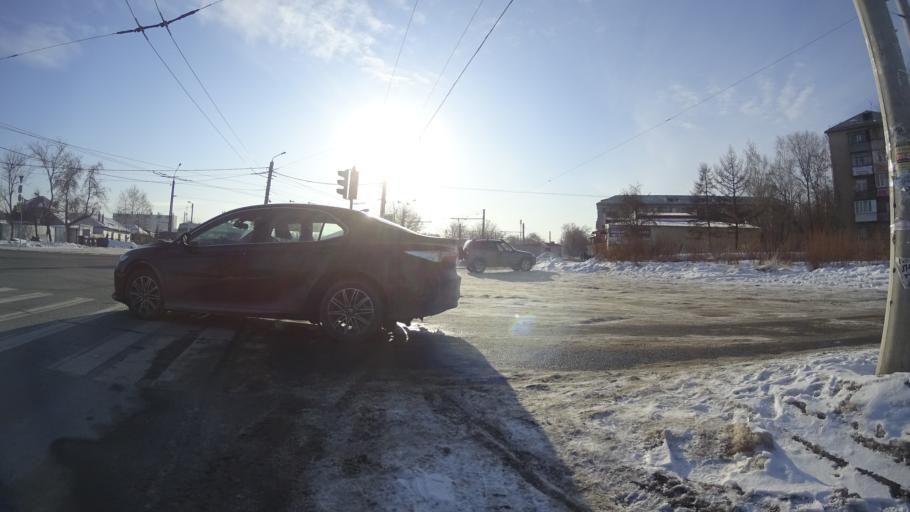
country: RU
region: Chelyabinsk
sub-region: Gorod Chelyabinsk
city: Chelyabinsk
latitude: 55.1840
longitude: 61.4585
